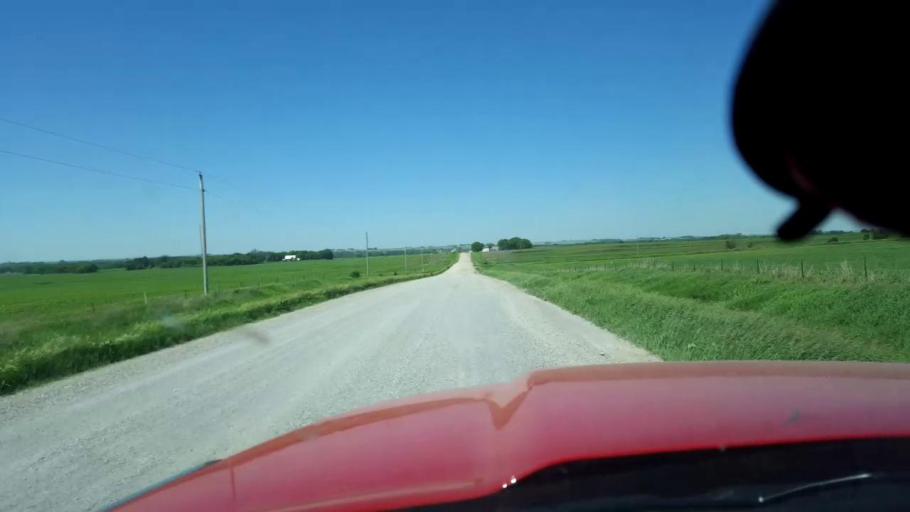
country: US
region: Iowa
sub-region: Chickasaw County
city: New Hampton
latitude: 43.2135
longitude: -92.2440
